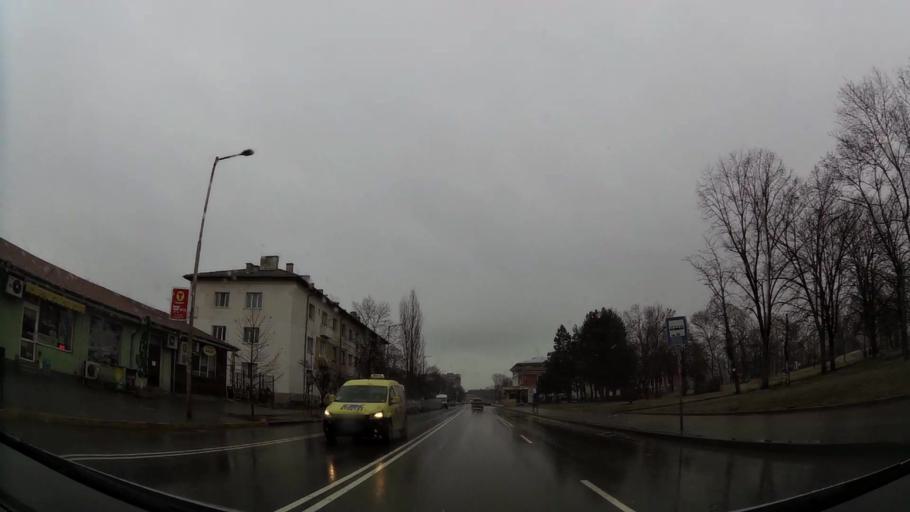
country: BG
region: Sofia-Capital
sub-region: Stolichna Obshtina
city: Sofia
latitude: 42.6647
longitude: 23.3991
